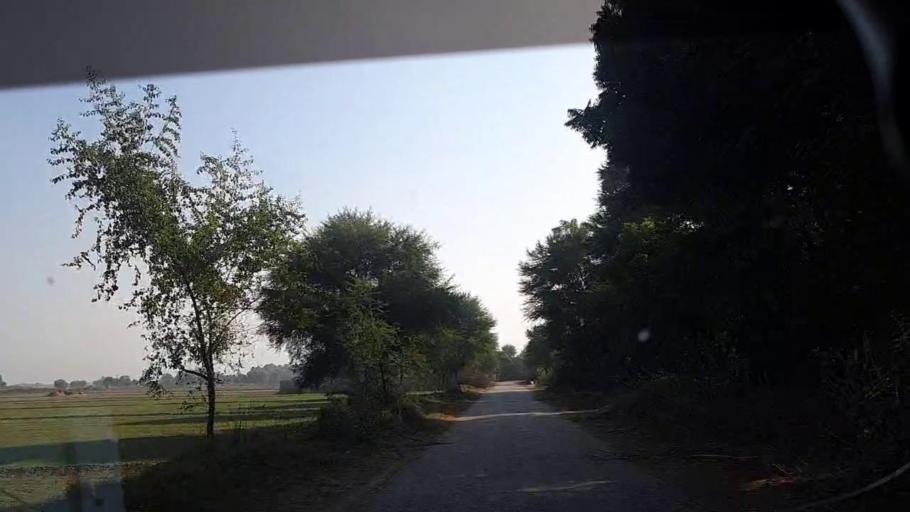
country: PK
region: Sindh
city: Hingorja
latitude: 27.2232
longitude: 68.2700
